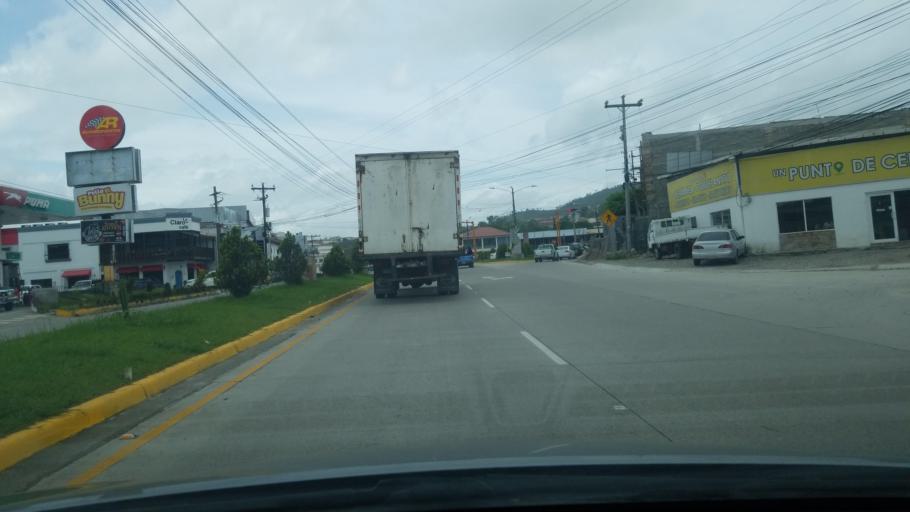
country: HN
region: Copan
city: Santa Rosa de Copan
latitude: 14.7805
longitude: -88.7797
